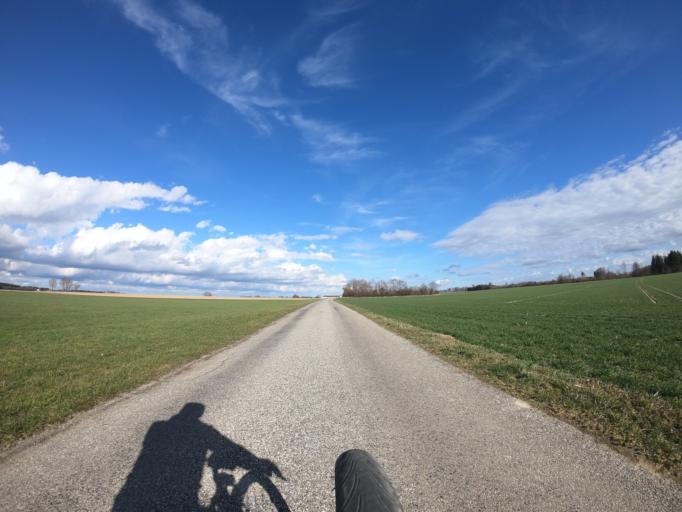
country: DE
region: Bavaria
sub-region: Upper Bavaria
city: Landsberied
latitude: 48.1829
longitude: 11.1987
